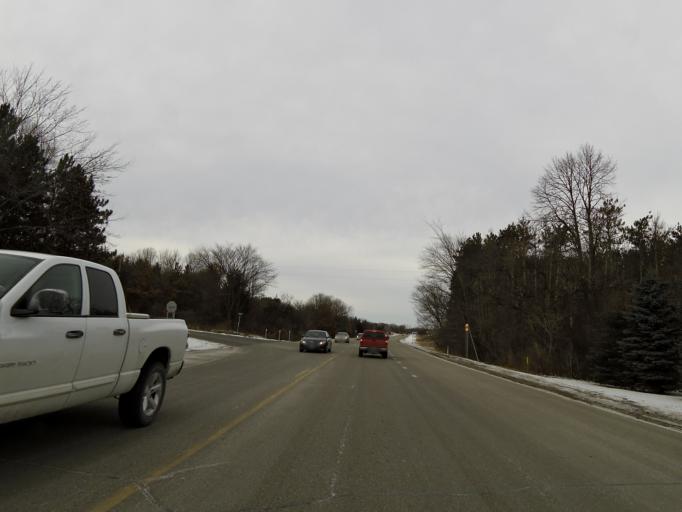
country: US
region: Wisconsin
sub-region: Saint Croix County
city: Hudson
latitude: 44.9795
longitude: -92.7775
